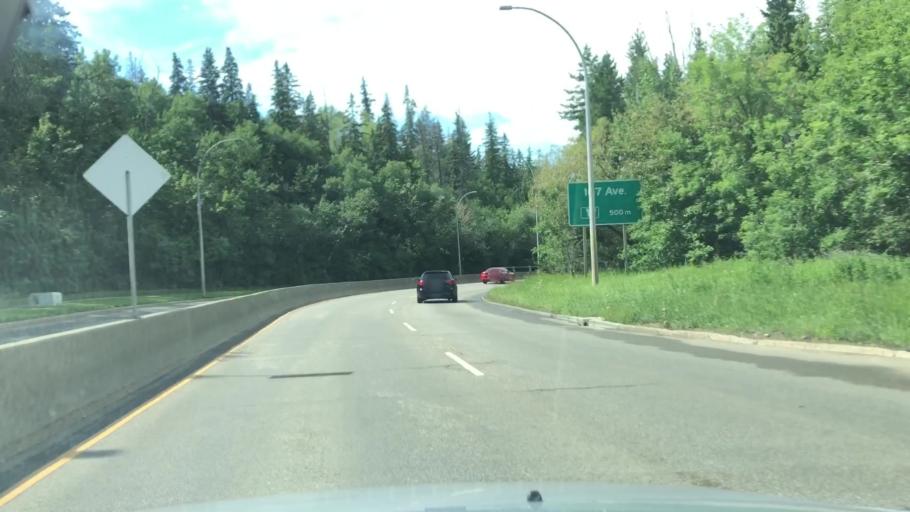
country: CA
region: Alberta
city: Edmonton
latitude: 53.5446
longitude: -113.5415
